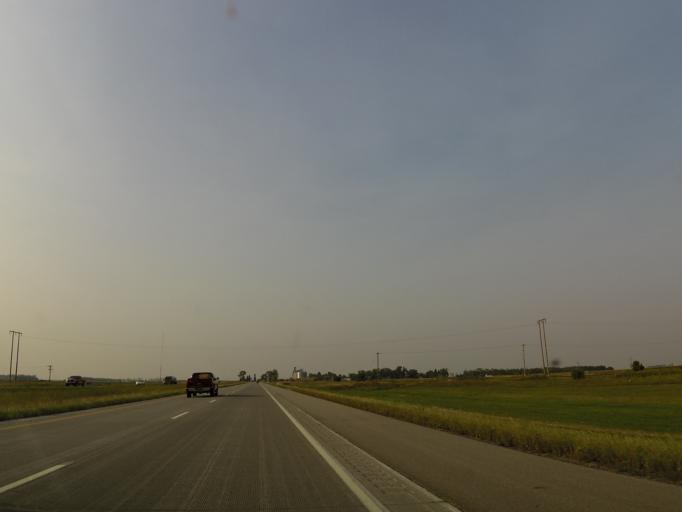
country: US
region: North Dakota
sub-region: Cass County
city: West Fargo
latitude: 47.1357
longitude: -96.9657
